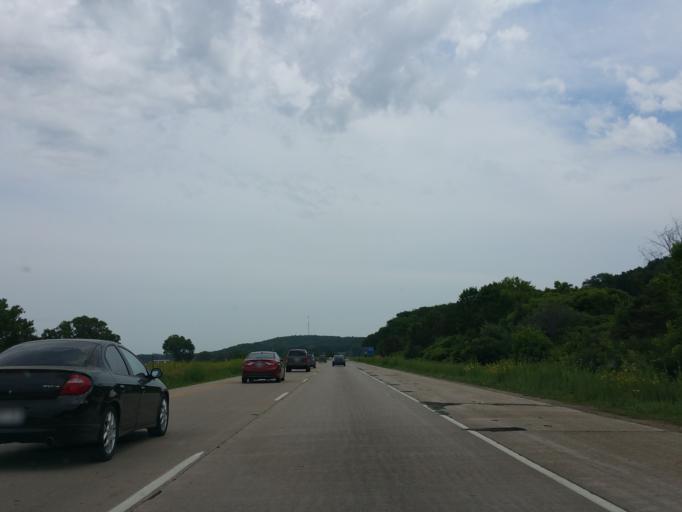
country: US
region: Wisconsin
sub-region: Columbia County
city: Portage
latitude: 43.4995
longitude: -89.5052
